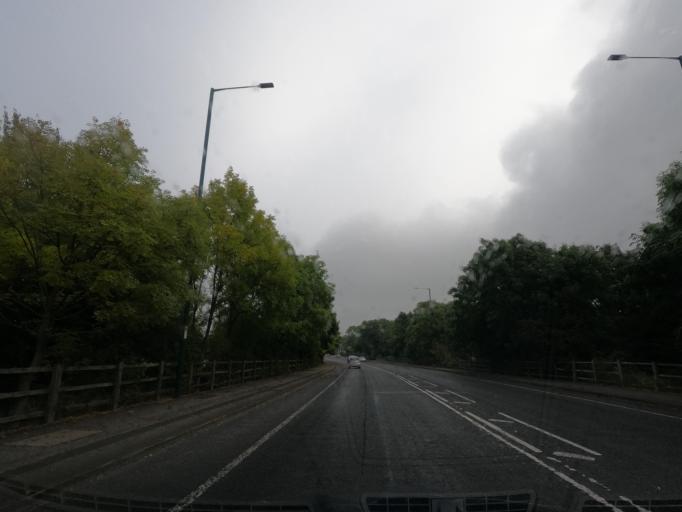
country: GB
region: England
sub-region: Redcar and Cleveland
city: South Bank
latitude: 54.5689
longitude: -1.1716
